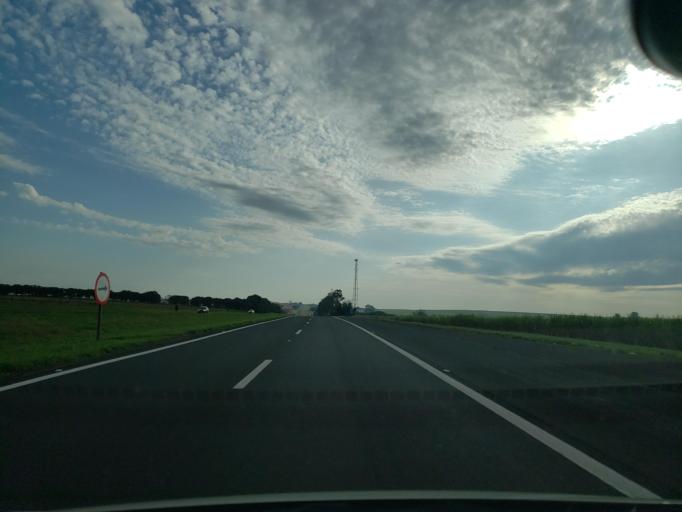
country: BR
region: Sao Paulo
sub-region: Valparaiso
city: Valparaiso
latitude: -21.2069
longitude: -50.7599
